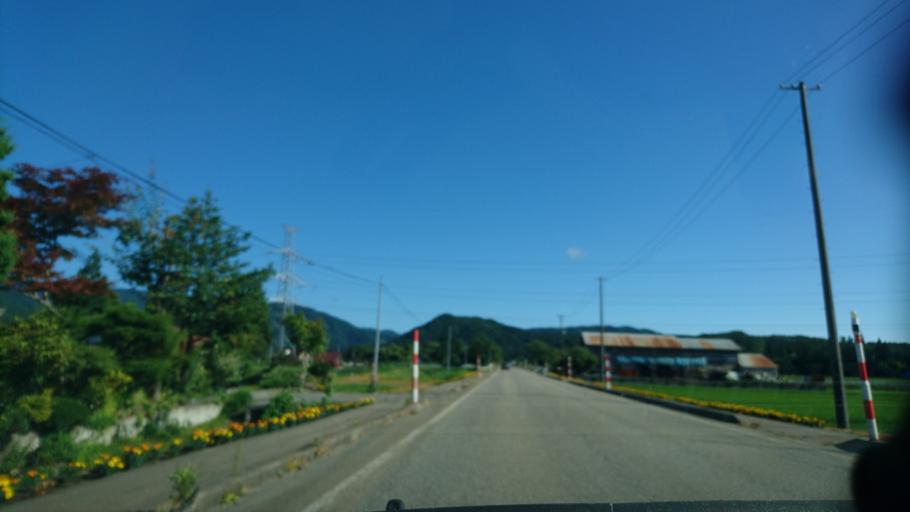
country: JP
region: Akita
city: Kakunodatemachi
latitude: 39.6638
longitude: 140.5692
